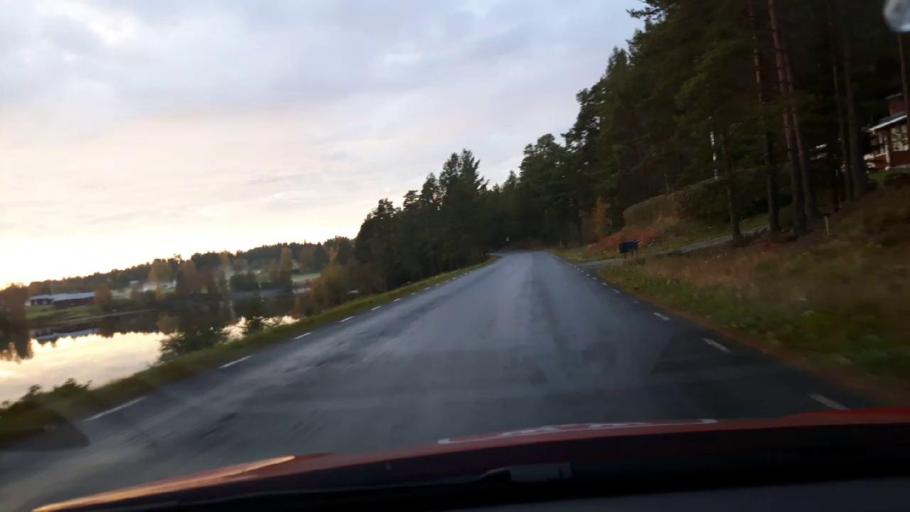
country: SE
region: Jaemtland
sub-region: OEstersunds Kommun
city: Lit
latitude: 63.3212
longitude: 14.9138
